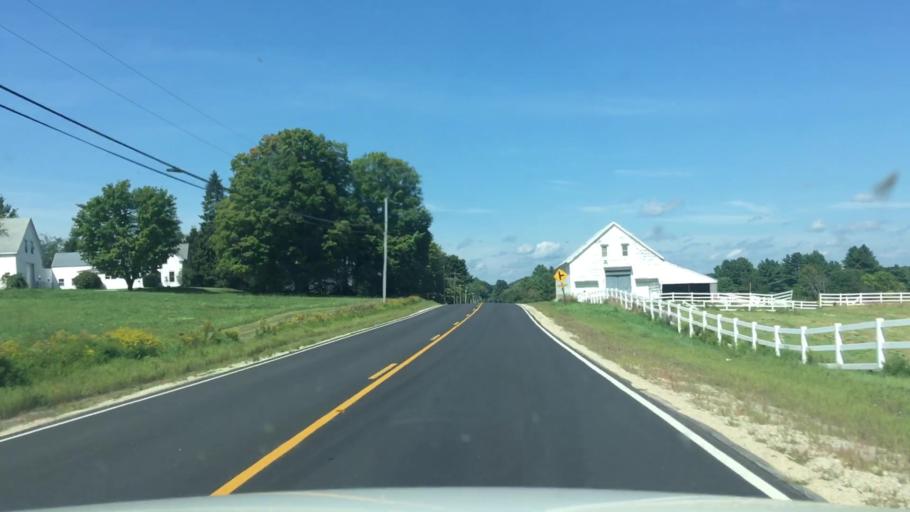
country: US
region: Maine
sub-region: Cumberland County
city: Cumberland Center
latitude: 43.7861
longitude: -70.3046
